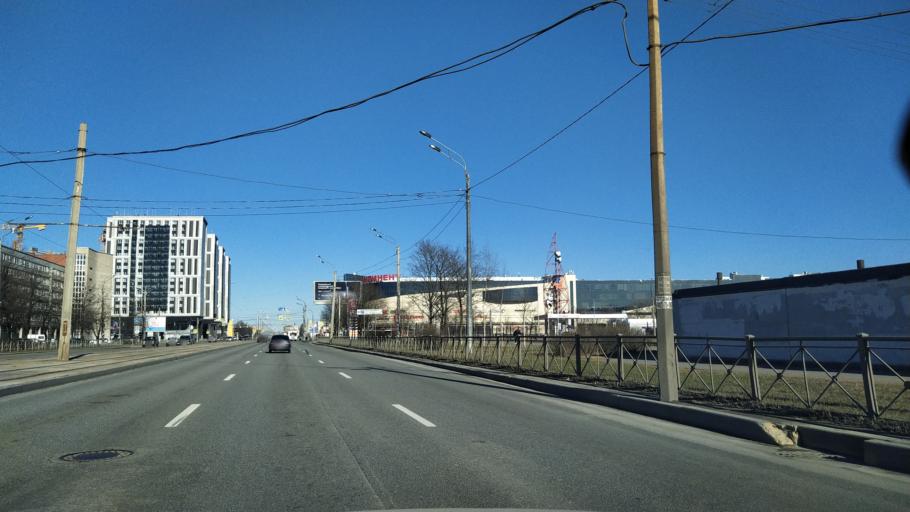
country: RU
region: St.-Petersburg
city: Kupchino
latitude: 59.8824
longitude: 30.3635
